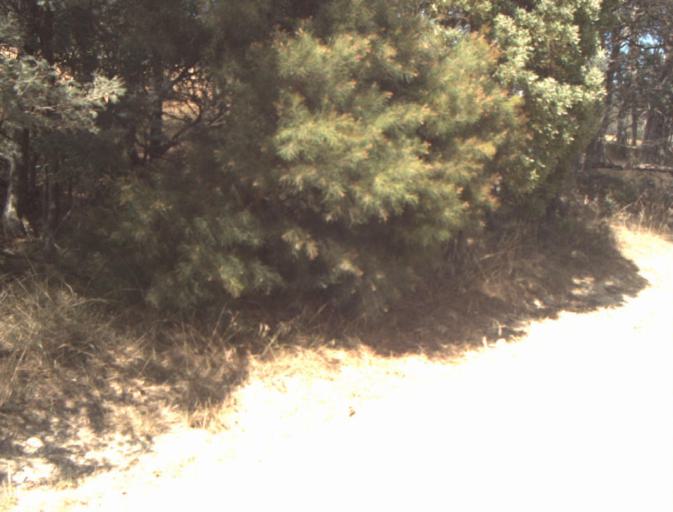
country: AU
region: Tasmania
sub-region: Launceston
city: Mayfield
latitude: -41.2564
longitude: 147.2108
